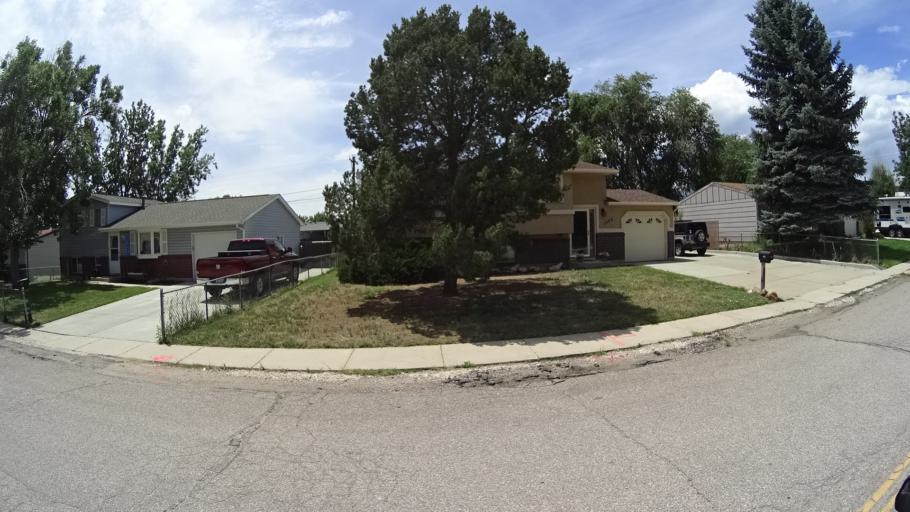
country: US
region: Colorado
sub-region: El Paso County
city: Security-Widefield
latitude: 38.7302
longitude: -104.7289
